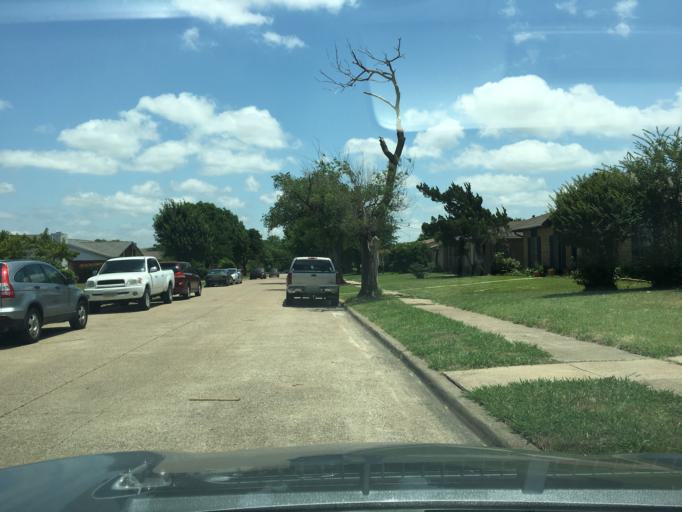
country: US
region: Texas
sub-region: Dallas County
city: Garland
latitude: 32.9523
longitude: -96.6704
